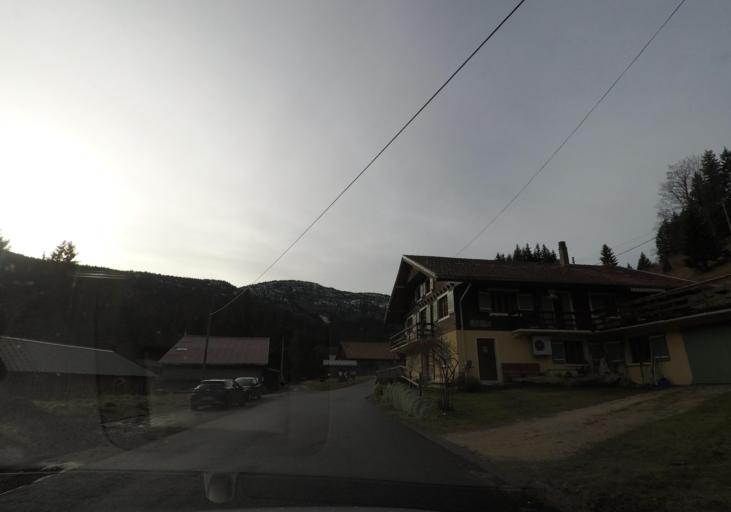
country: FR
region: Rhone-Alpes
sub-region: Departement de la Haute-Savoie
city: Ayse
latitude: 46.0385
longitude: 6.4422
